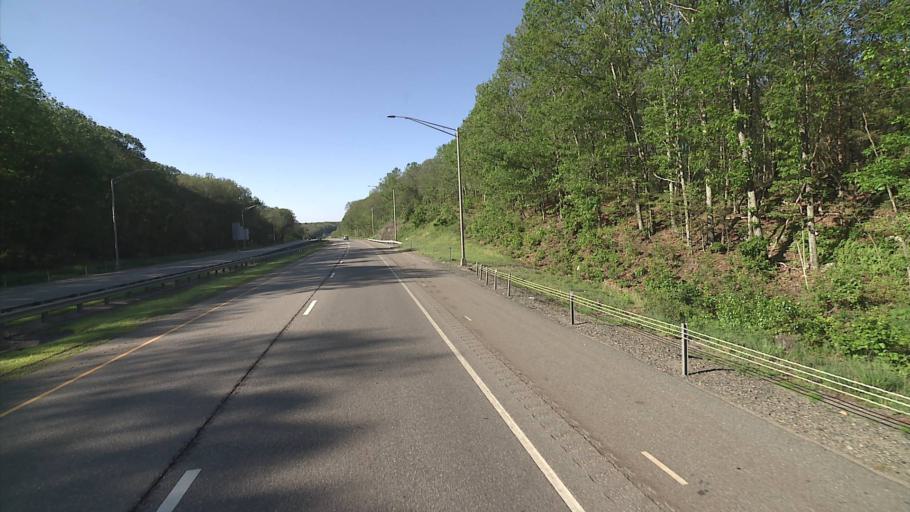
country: US
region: Connecticut
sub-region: Windham County
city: Wauregan
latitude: 41.7502
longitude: -71.8793
